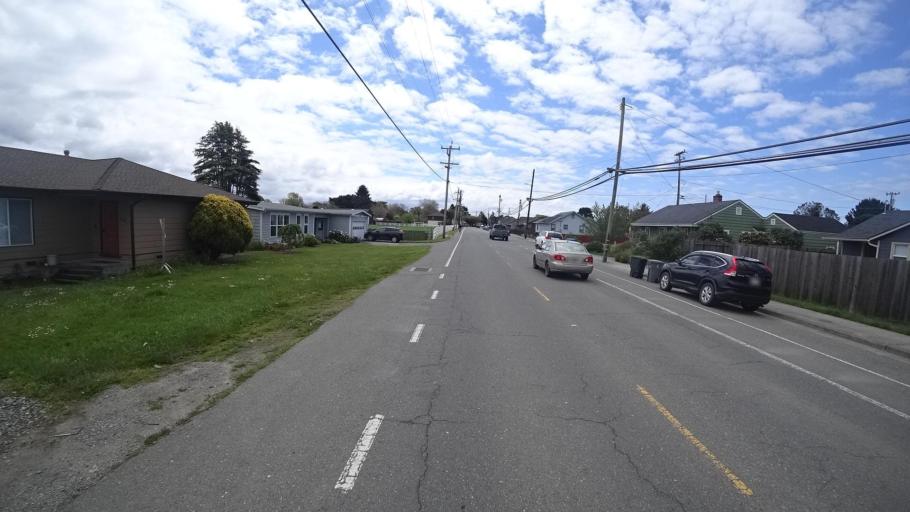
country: US
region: California
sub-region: Humboldt County
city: Arcata
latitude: 40.8885
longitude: -124.0880
